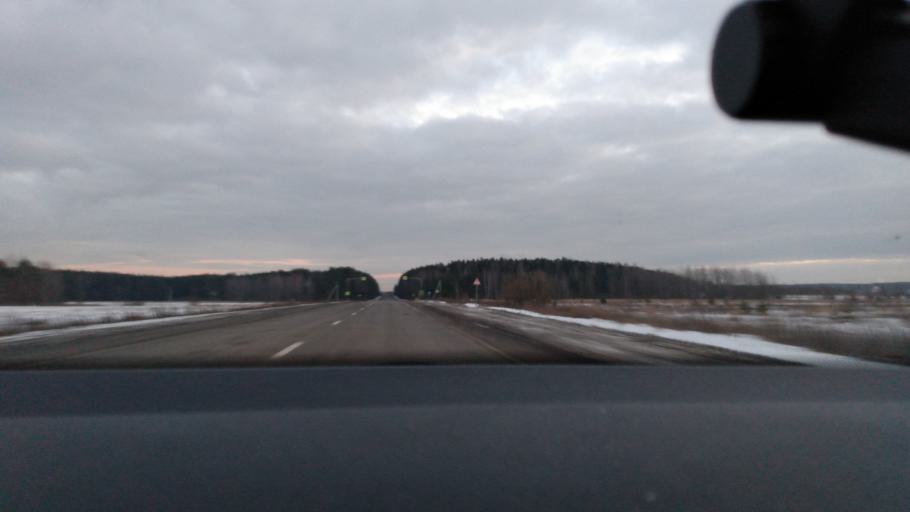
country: RU
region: Moskovskaya
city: Yegor'yevsk
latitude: 55.4355
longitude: 39.0249
